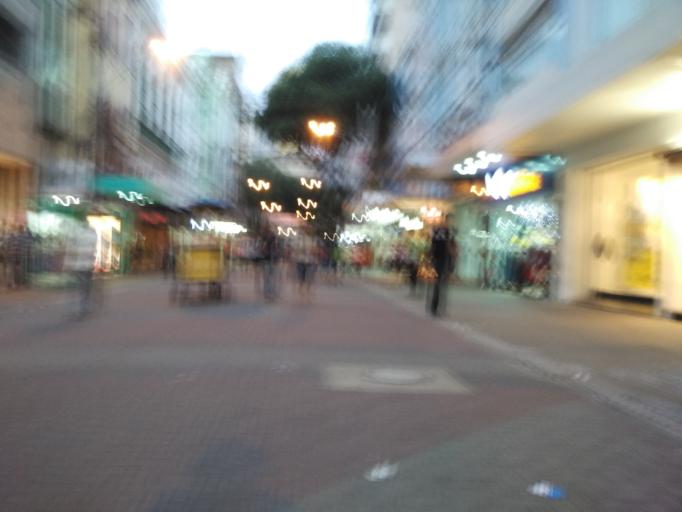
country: BR
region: Pernambuco
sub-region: Recife
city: Recife
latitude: -8.0642
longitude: -34.8799
